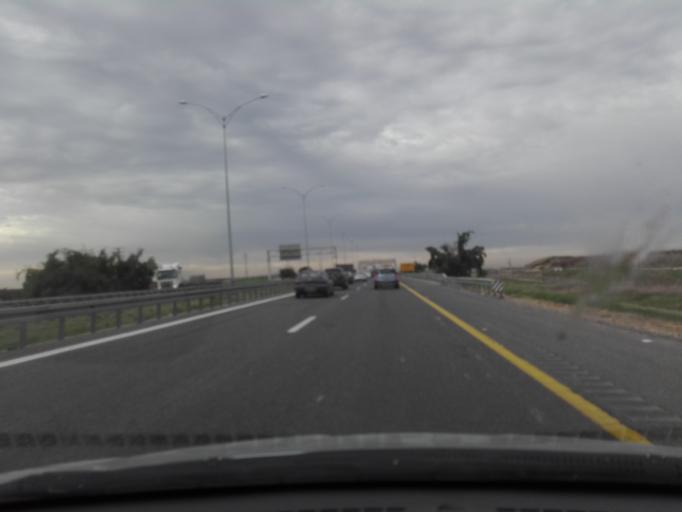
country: IL
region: Central District
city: Ramla
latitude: 31.8926
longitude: 34.8820
